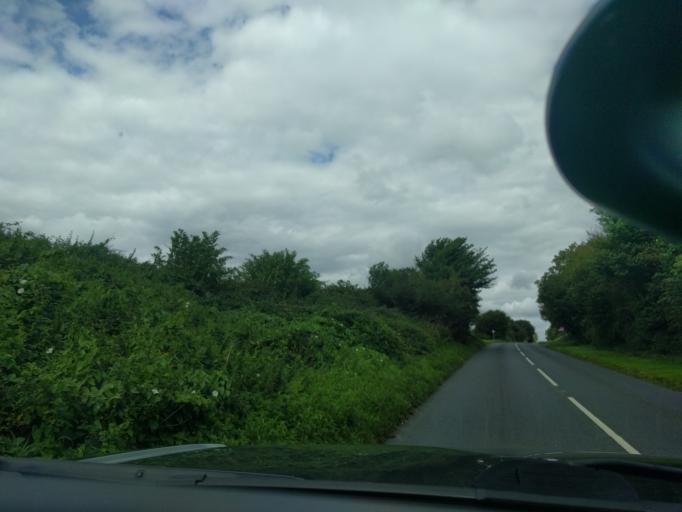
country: GB
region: England
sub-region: Wiltshire
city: Atworth
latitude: 51.4039
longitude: -2.1653
